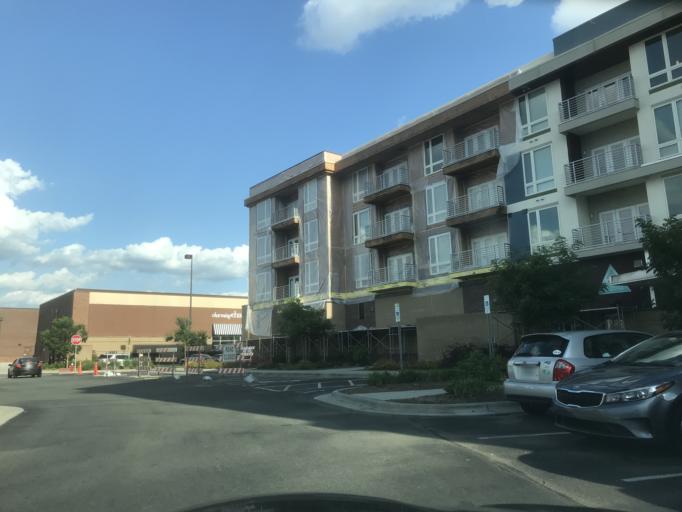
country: US
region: North Carolina
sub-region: Wake County
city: Morrisville
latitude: 35.8077
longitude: -78.8183
